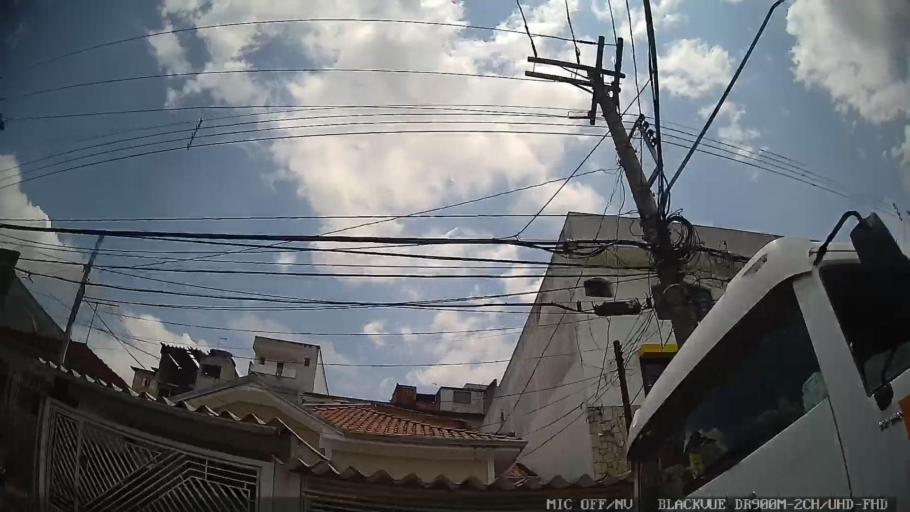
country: BR
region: Sao Paulo
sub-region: Osasco
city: Osasco
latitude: -23.4855
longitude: -46.7159
